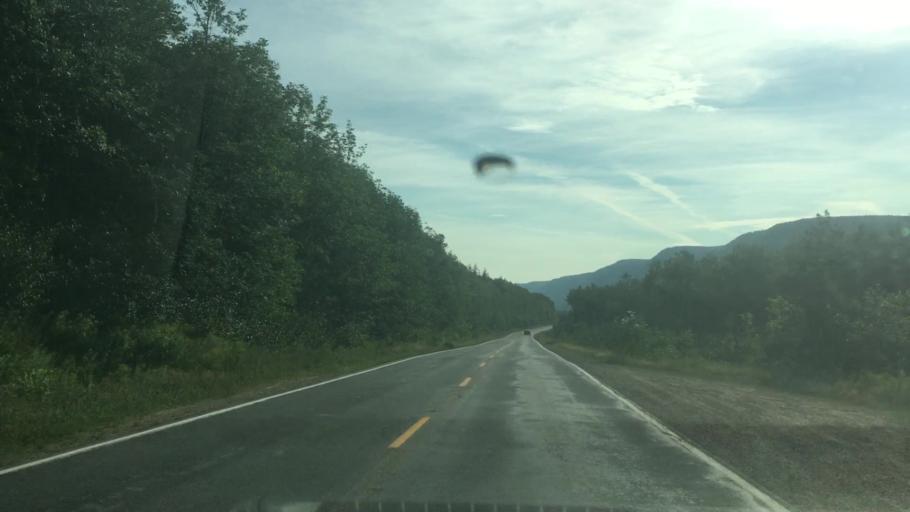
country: CA
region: Nova Scotia
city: Sydney Mines
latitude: 46.8631
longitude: -60.5640
